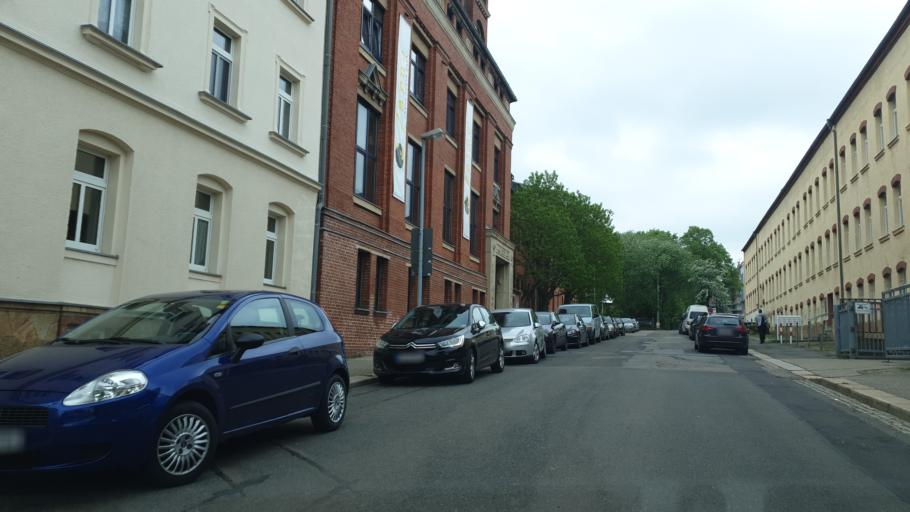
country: DE
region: Saxony
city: Chemnitz
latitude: 50.8358
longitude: 12.8914
